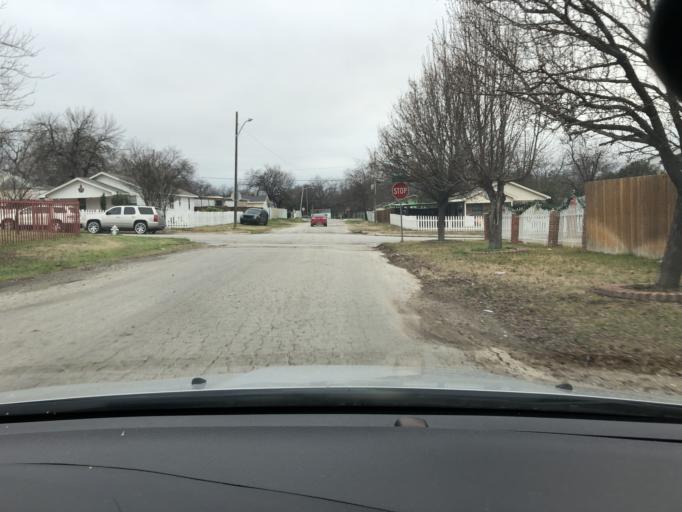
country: US
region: Texas
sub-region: Tarrant County
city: Fort Worth
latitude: 32.7257
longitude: -97.2811
